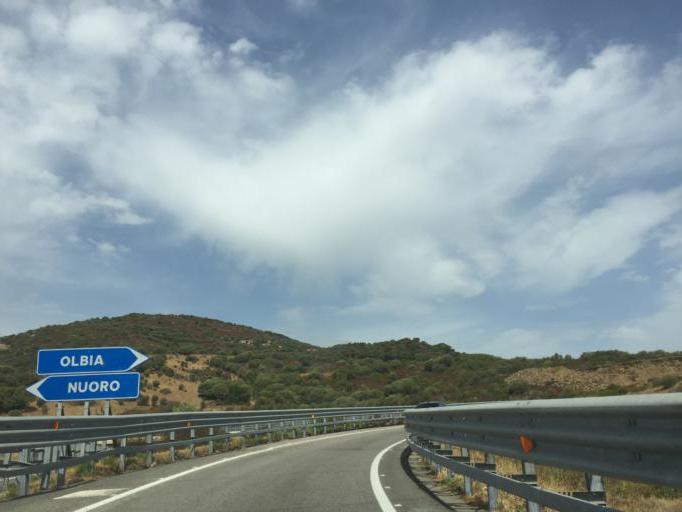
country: IT
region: Sardinia
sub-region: Provincia di Olbia-Tempio
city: San Teodoro
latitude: 40.7584
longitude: 9.6428
